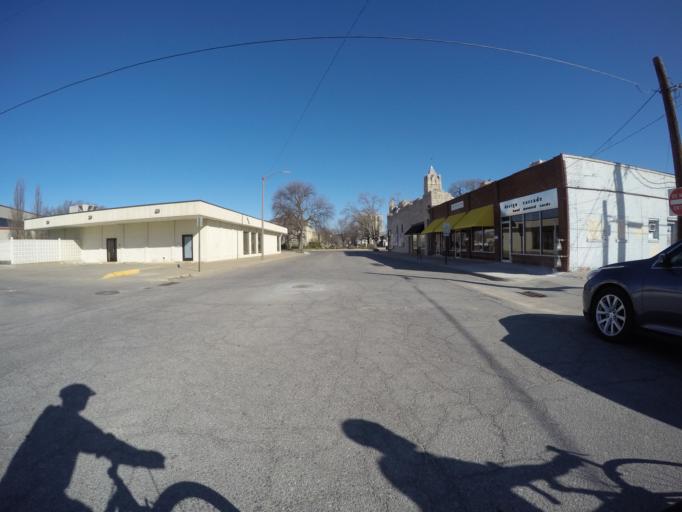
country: US
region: Kansas
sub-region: Riley County
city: Manhattan
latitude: 39.1788
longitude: -96.5635
